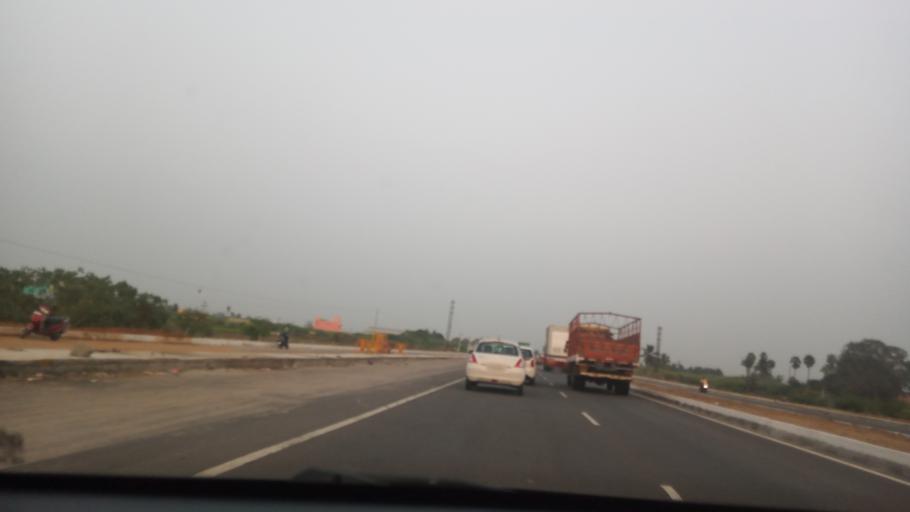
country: IN
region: Tamil Nadu
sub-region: Vellore
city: Walajapet
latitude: 12.9018
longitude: 79.4666
